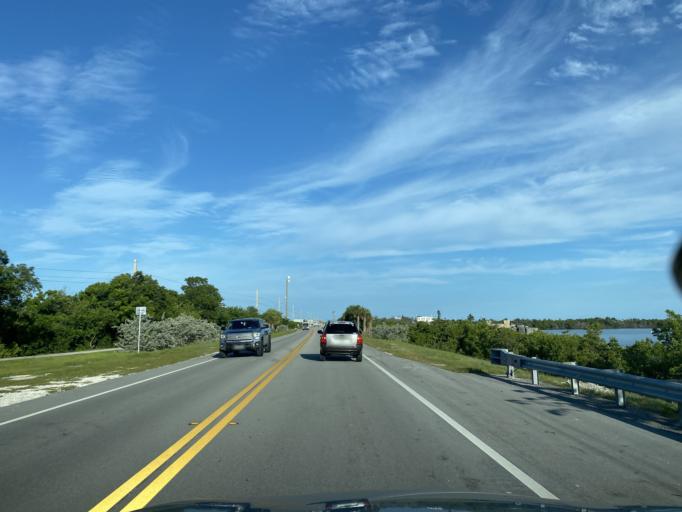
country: US
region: Florida
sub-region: Monroe County
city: Cudjoe Key
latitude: 24.6608
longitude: -81.4369
